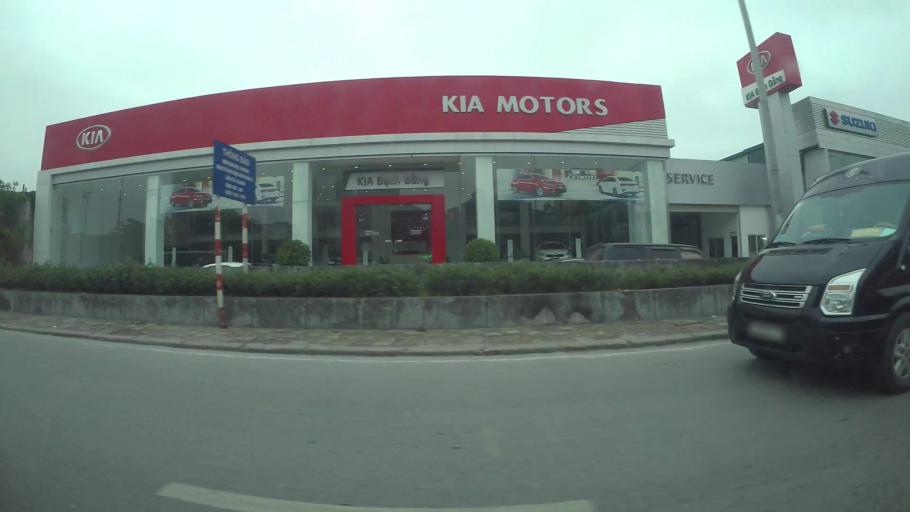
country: VN
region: Ha Noi
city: Hai BaTrung
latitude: 21.0050
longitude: 105.8696
